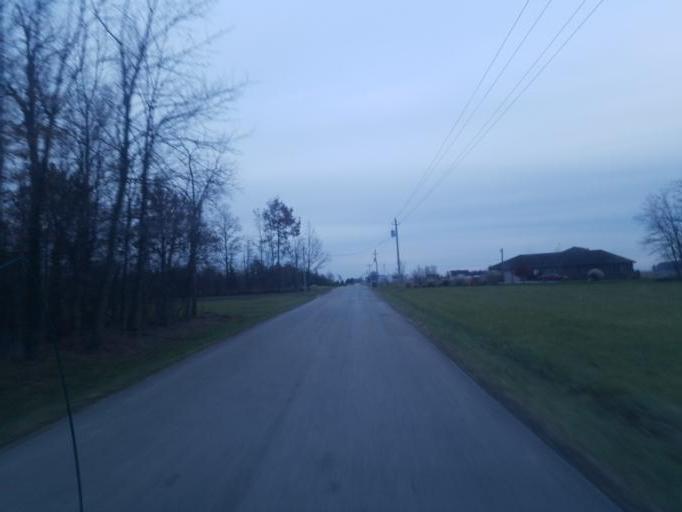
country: US
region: Indiana
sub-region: Adams County
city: Decatur
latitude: 40.7663
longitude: -85.0141
